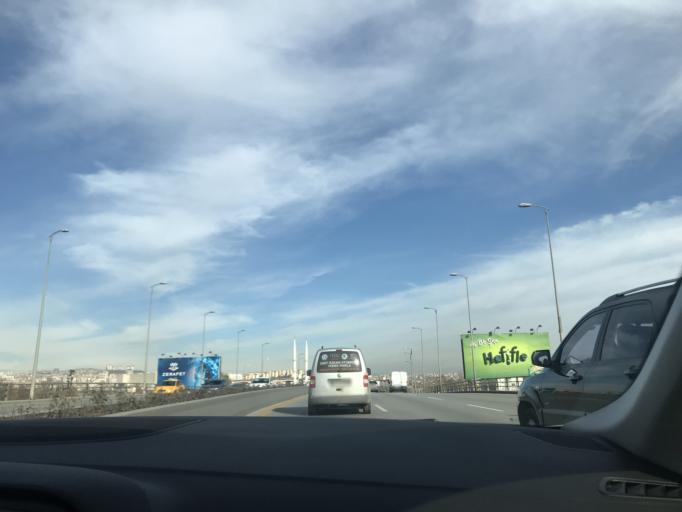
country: TR
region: Ankara
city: Ankara
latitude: 39.9506
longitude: 32.8352
